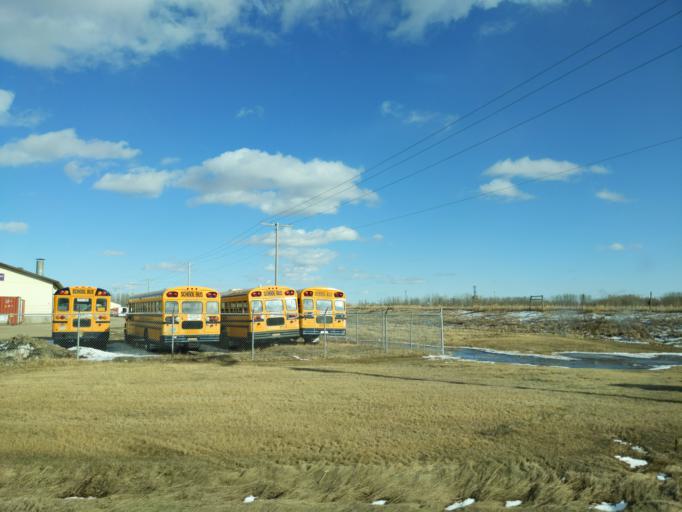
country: CA
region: Saskatchewan
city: Lloydminster
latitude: 53.2753
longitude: -109.9710
